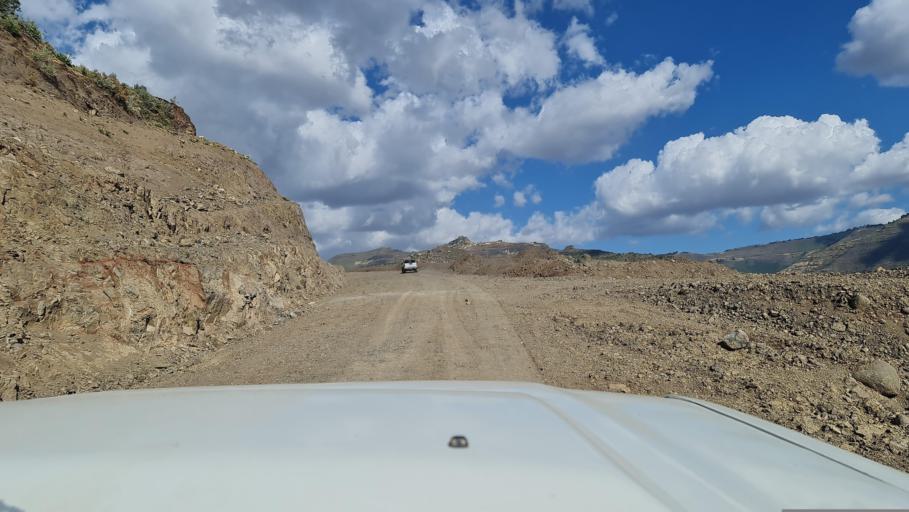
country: ET
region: Amhara
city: Debark'
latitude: 13.1179
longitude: 38.0211
